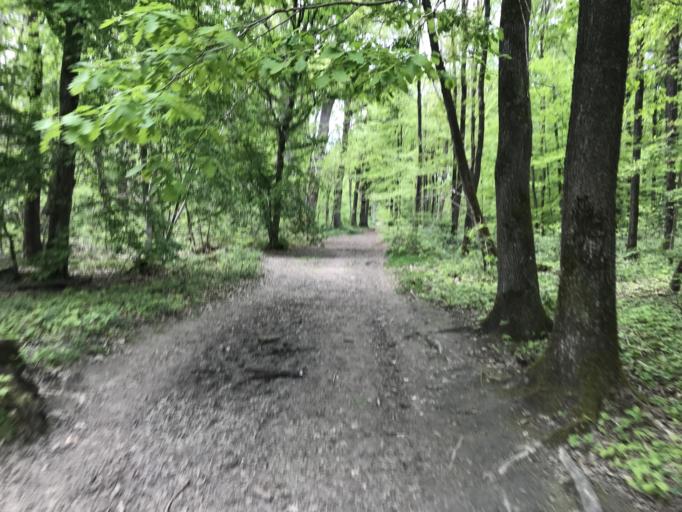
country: FR
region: Ile-de-France
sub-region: Departement de l'Essonne
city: Bievres
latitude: 48.7575
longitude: 2.2351
